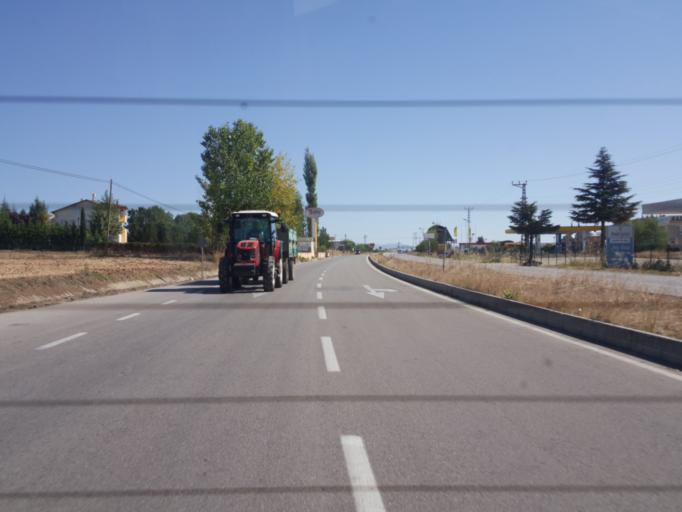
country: TR
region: Tokat
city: Zile
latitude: 40.3094
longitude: 35.9050
